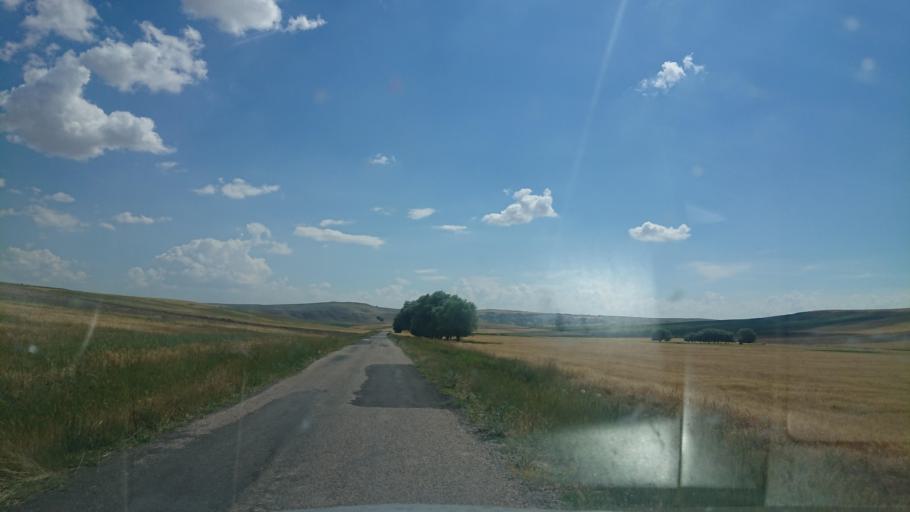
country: TR
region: Aksaray
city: Agacoren
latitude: 38.7945
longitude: 33.8214
